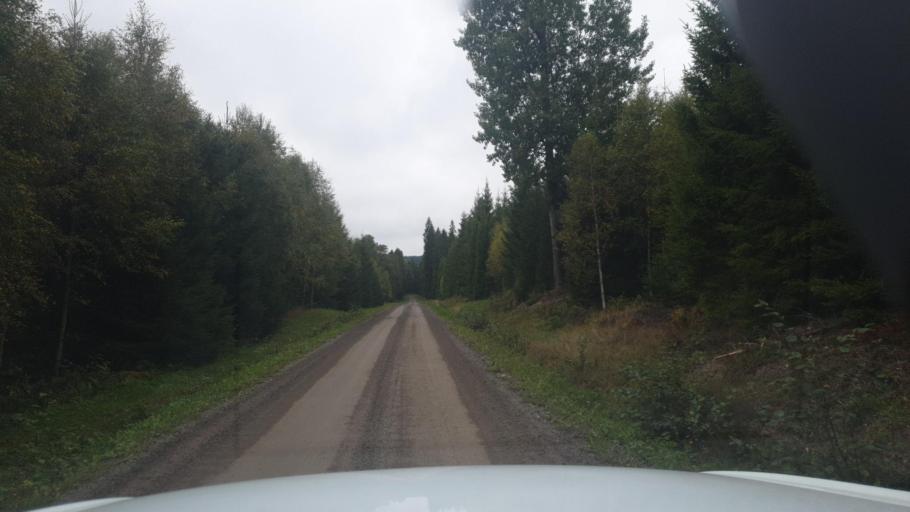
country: SE
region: Vaermland
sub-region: Sunne Kommun
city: Sunne
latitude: 59.8572
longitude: 12.8620
